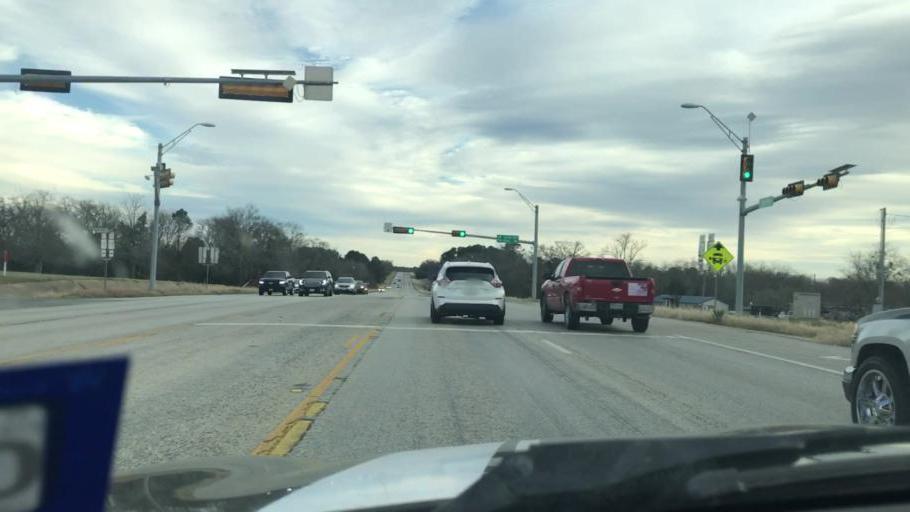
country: US
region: Texas
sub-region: Bastrop County
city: Camp Swift
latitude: 30.2797
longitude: -97.2425
